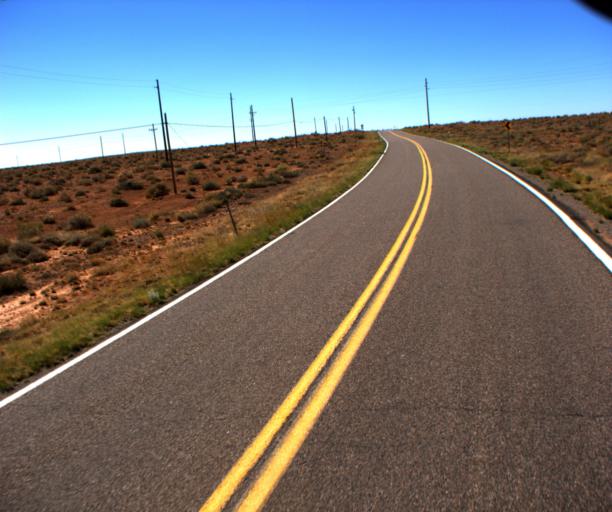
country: US
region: Arizona
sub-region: Coconino County
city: LeChee
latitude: 35.0845
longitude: -110.8631
